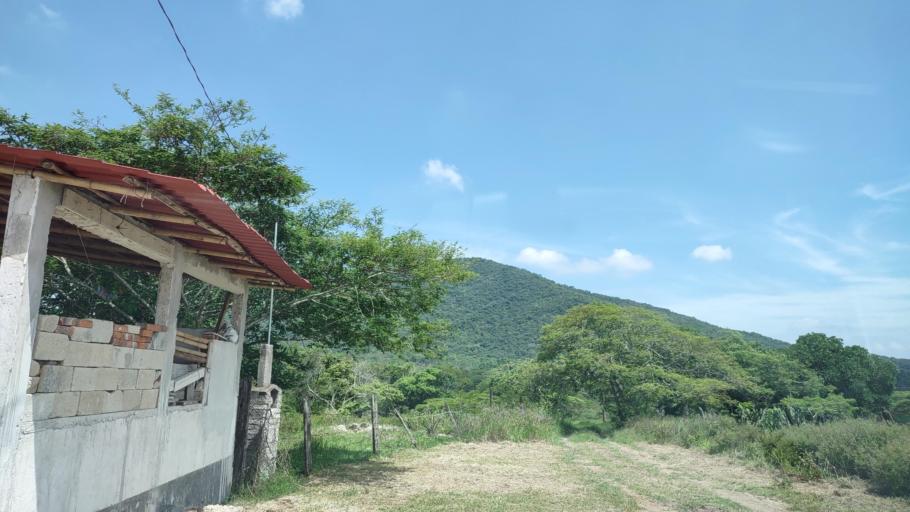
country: MX
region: Veracruz
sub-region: Coatepec
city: Bella Esperanza
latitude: 19.4270
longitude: -96.8096
